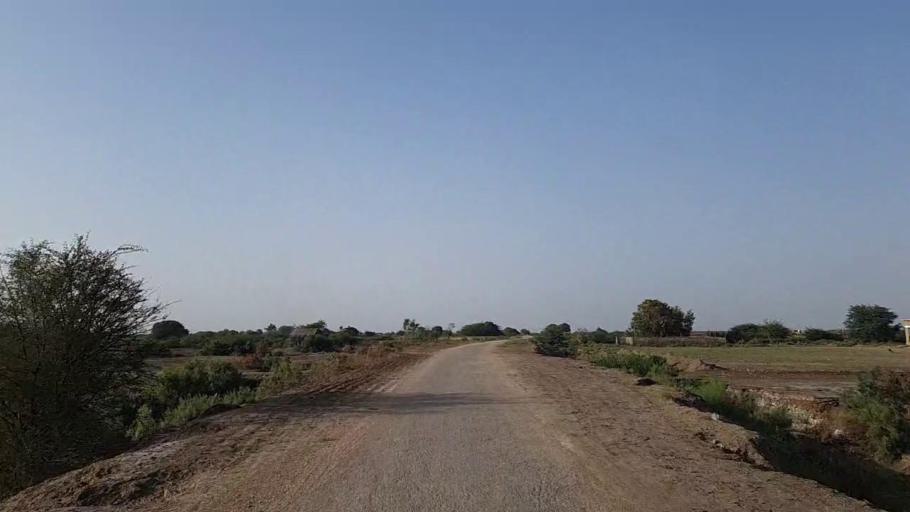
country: PK
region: Sindh
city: Jati
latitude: 24.3127
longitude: 68.1690
